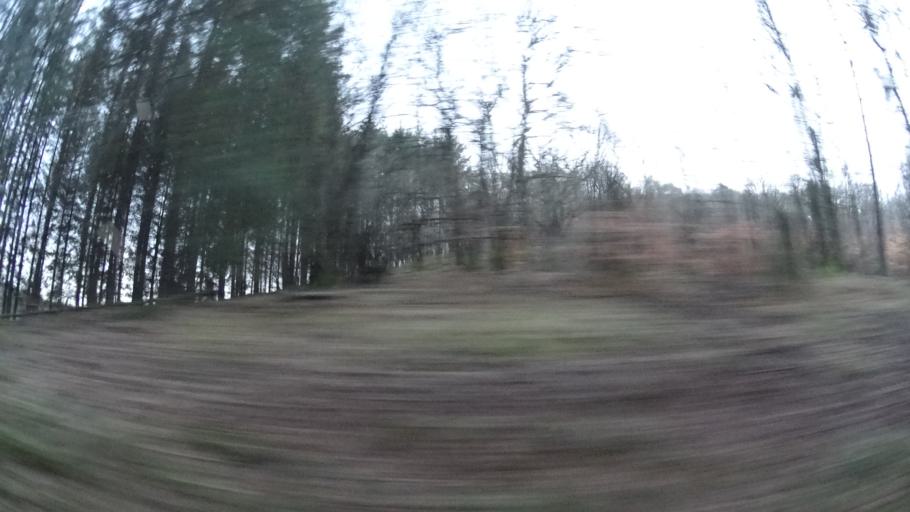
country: DE
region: Rheinland-Pfalz
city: Dambach
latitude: 49.6210
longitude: 7.1268
